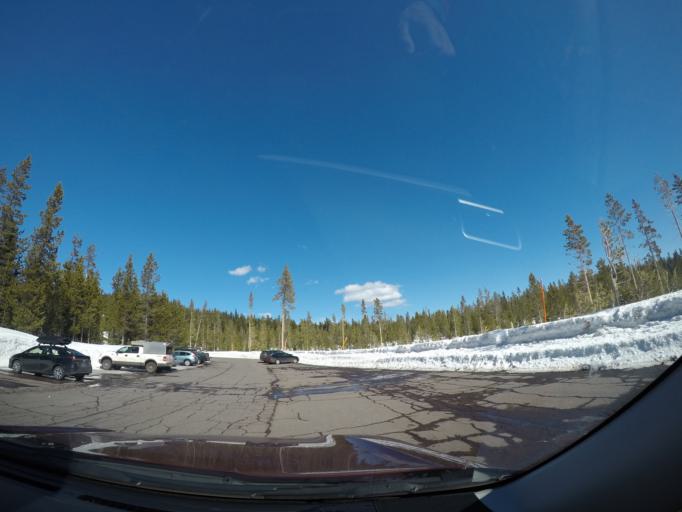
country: US
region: Oregon
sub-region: Deschutes County
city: Sunriver
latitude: 43.9894
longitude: -121.5677
